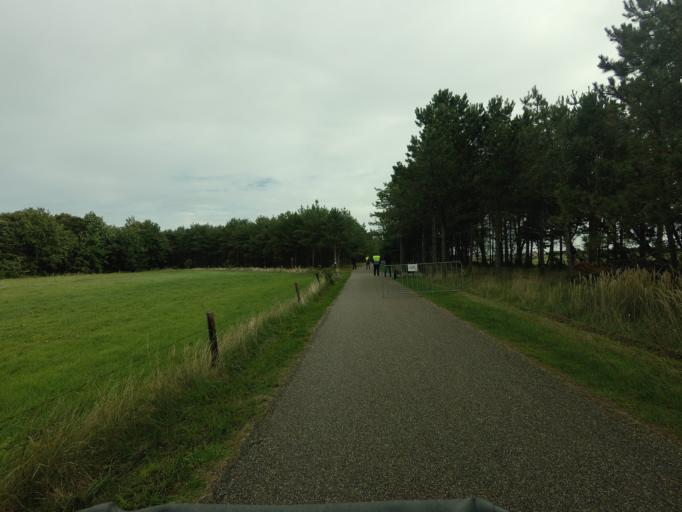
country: NL
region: Friesland
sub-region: Gemeente Ameland
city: Nes
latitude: 53.4524
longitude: 5.7844
